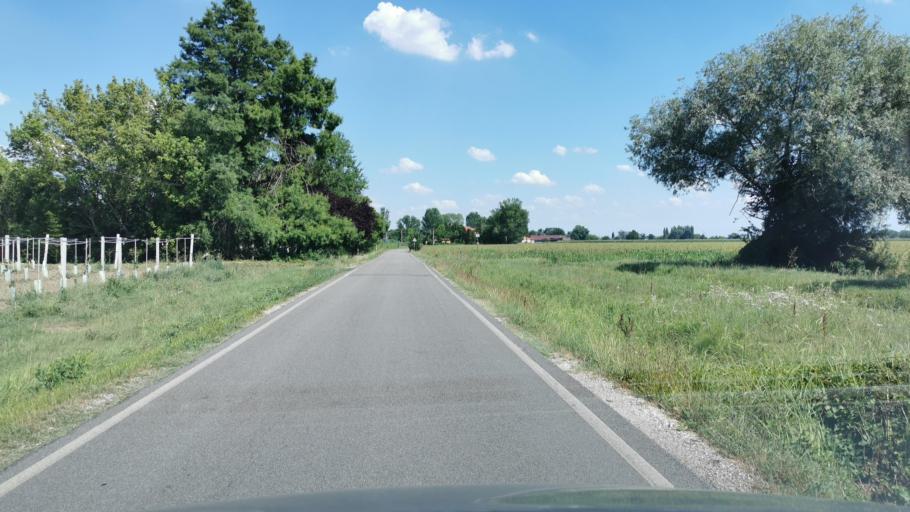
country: IT
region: Emilia-Romagna
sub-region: Provincia di Modena
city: Fossoli
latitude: 44.8146
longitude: 10.8963
